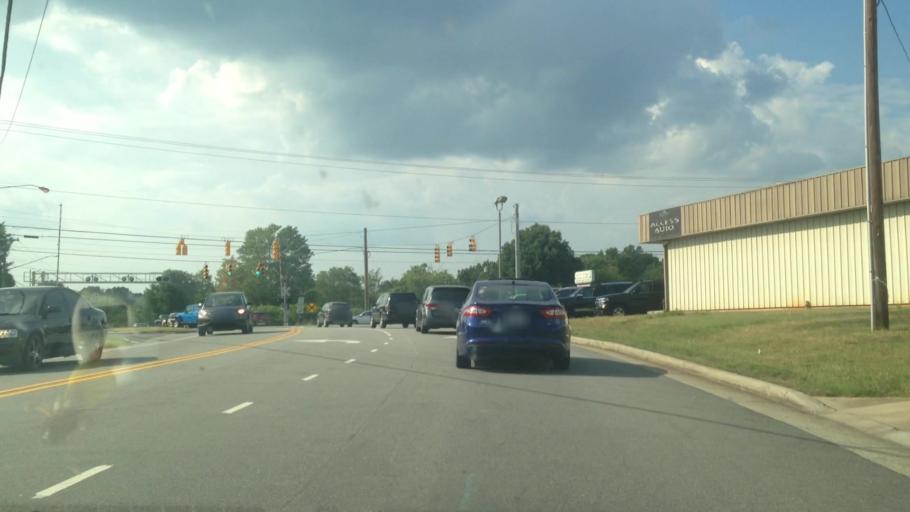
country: US
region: North Carolina
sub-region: Forsyth County
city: Kernersville
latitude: 36.1334
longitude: -80.1177
